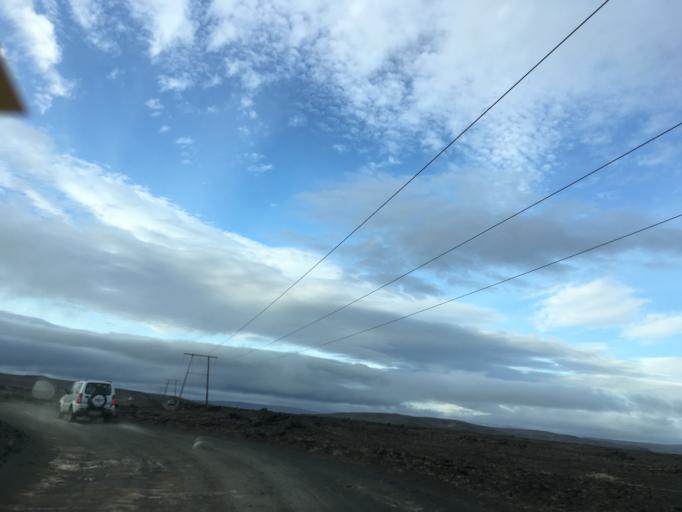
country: IS
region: South
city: Vestmannaeyjar
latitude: 64.1367
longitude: -19.1268
